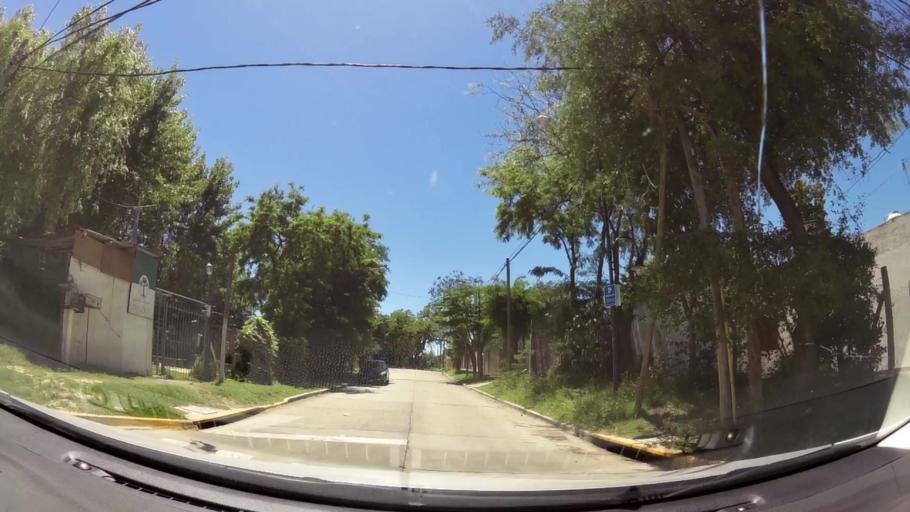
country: AR
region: Buenos Aires
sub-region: Partido de Tigre
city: Tigre
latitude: -34.4547
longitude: -58.5513
